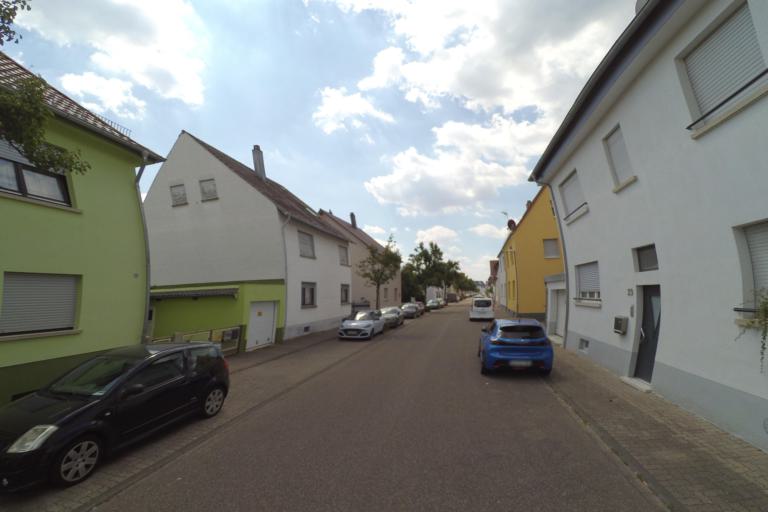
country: DE
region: Baden-Wuerttemberg
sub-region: Karlsruhe Region
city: Eggenstein-Leopoldshafen
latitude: 49.0775
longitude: 8.3967
